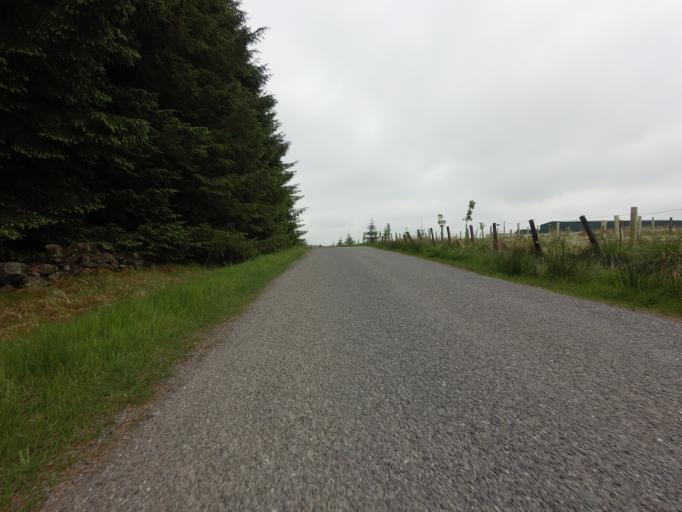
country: GB
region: Scotland
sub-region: Perth and Kinross
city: Kinross
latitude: 56.1484
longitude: -3.4522
